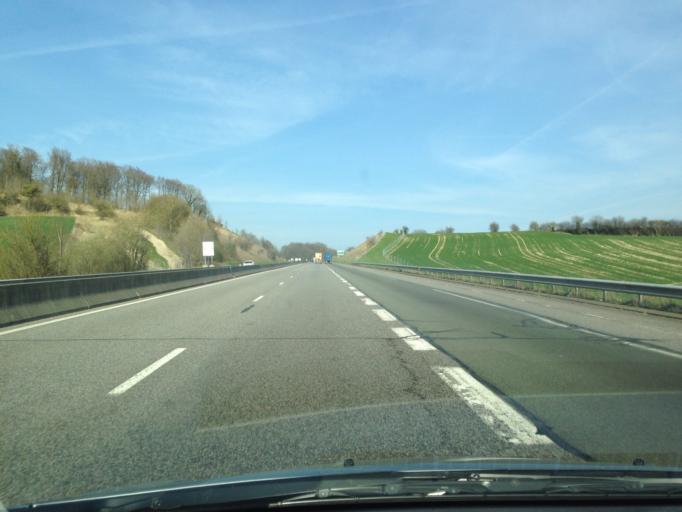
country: FR
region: Haute-Normandie
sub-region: Departement de la Seine-Maritime
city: Neufchatel-en-Bray
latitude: 49.7301
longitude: 1.4599
